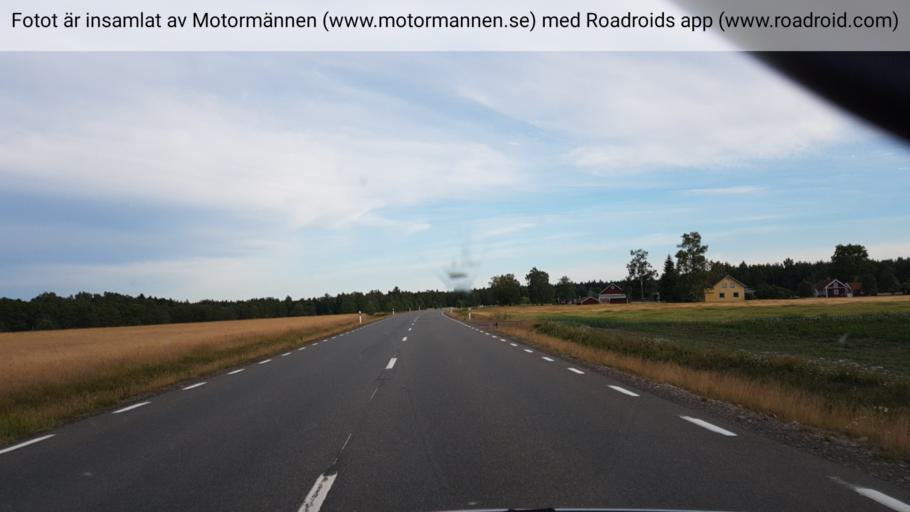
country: SE
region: Vaestra Goetaland
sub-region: Tibro Kommun
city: Tibro
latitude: 58.4881
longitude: 14.1683
